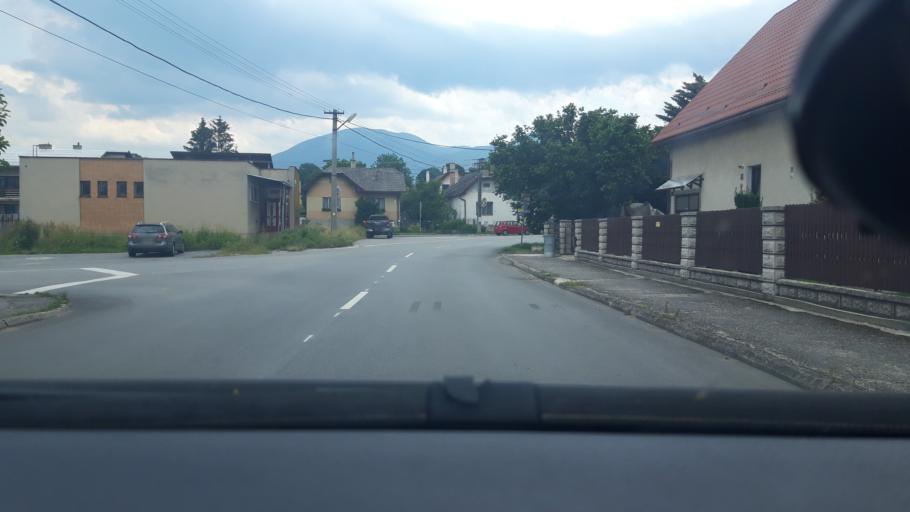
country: SK
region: Zilinsky
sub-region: Okres Martin
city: Martin
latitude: 48.9127
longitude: 18.8843
